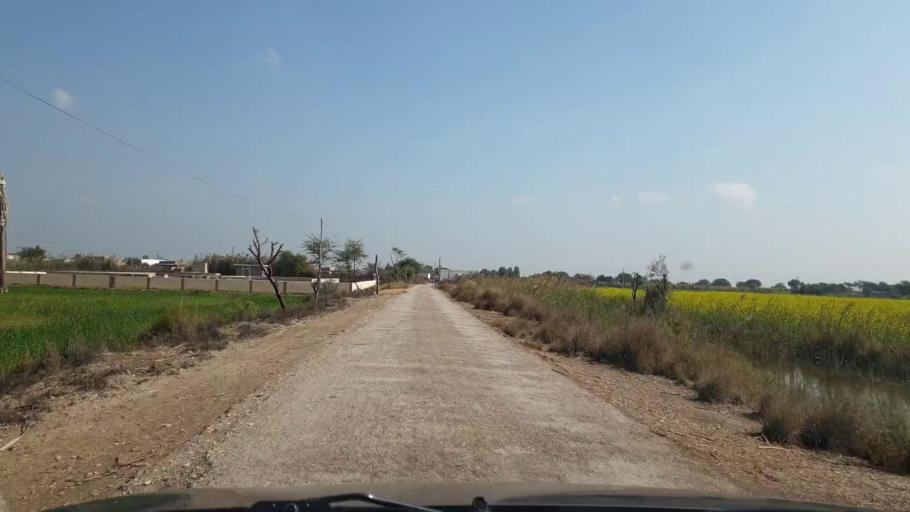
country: PK
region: Sindh
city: Sinjhoro
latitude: 26.0599
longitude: 68.7534
